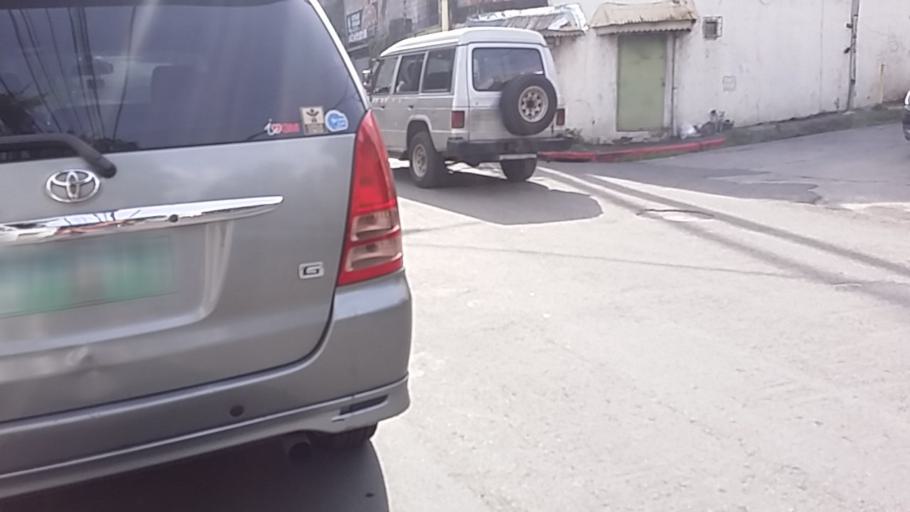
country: PH
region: Metro Manila
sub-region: Mandaluyong
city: Mandaluyong City
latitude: 14.5922
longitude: 121.0389
